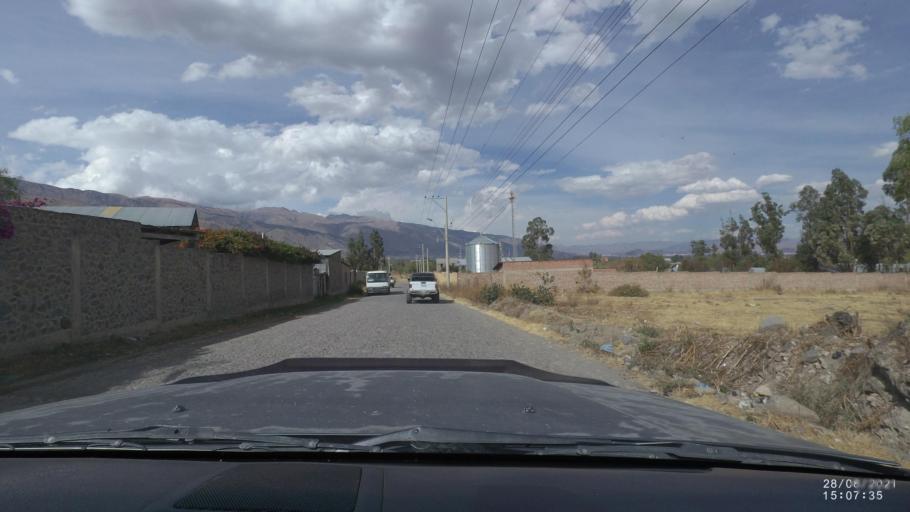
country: BO
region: Cochabamba
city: Cochabamba
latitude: -17.3369
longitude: -66.2807
